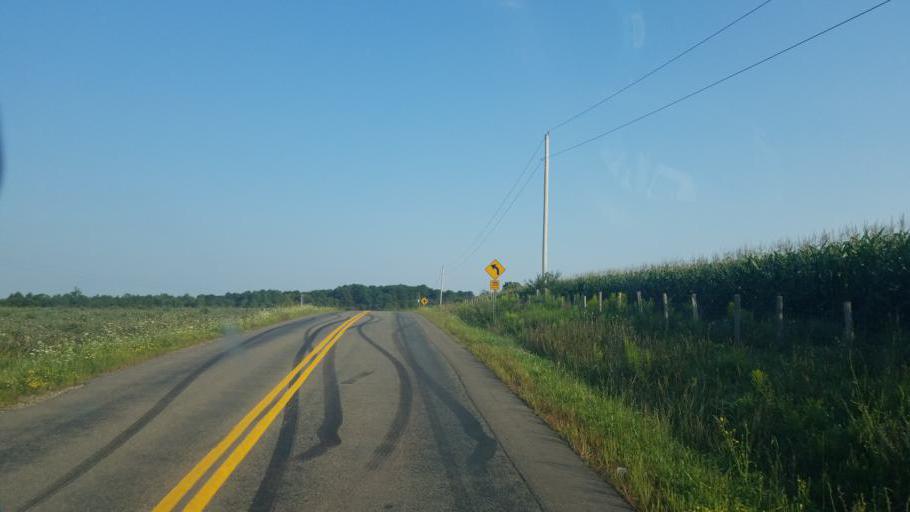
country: US
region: New York
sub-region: Allegany County
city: Andover
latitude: 42.0724
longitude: -77.6367
